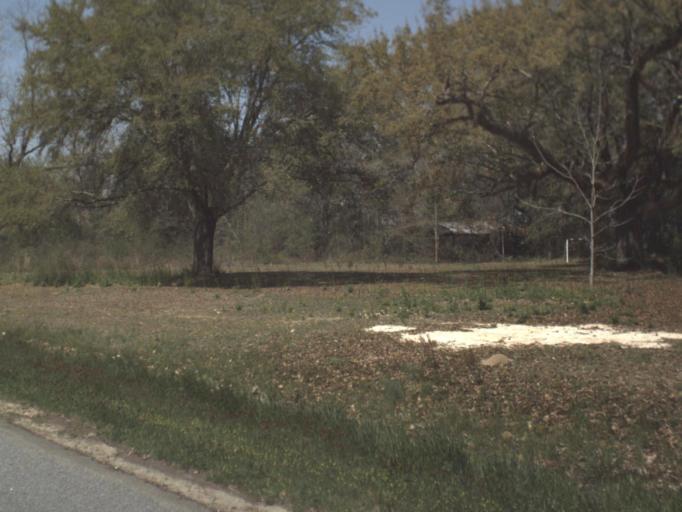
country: US
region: Alabama
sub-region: Geneva County
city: Geneva
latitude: 30.9497
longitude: -85.7425
